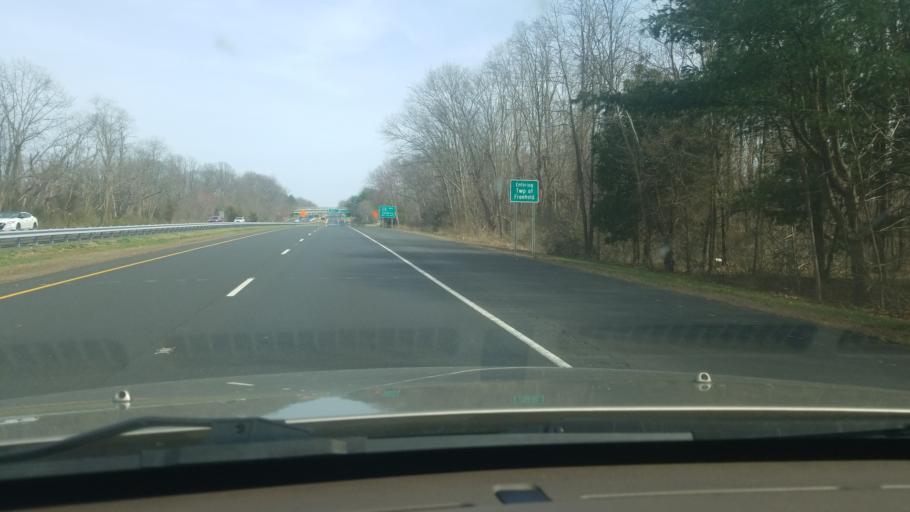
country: US
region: New Jersey
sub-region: Monmouth County
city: West Freehold
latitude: 40.2520
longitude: -74.3187
